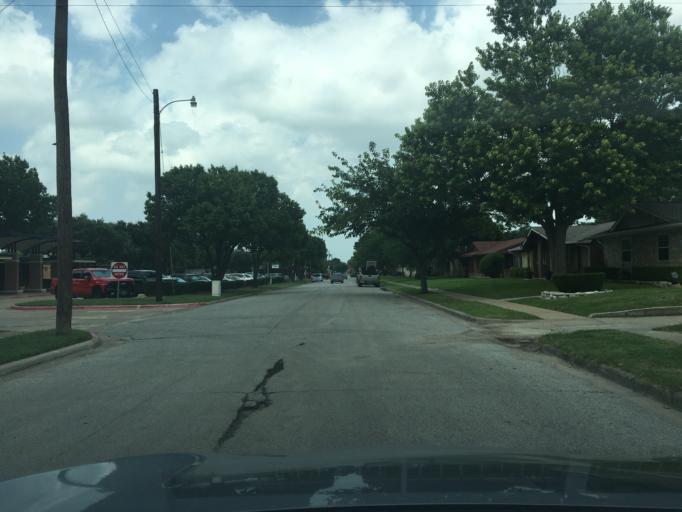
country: US
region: Texas
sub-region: Dallas County
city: Richardson
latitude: 32.9134
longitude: -96.6919
